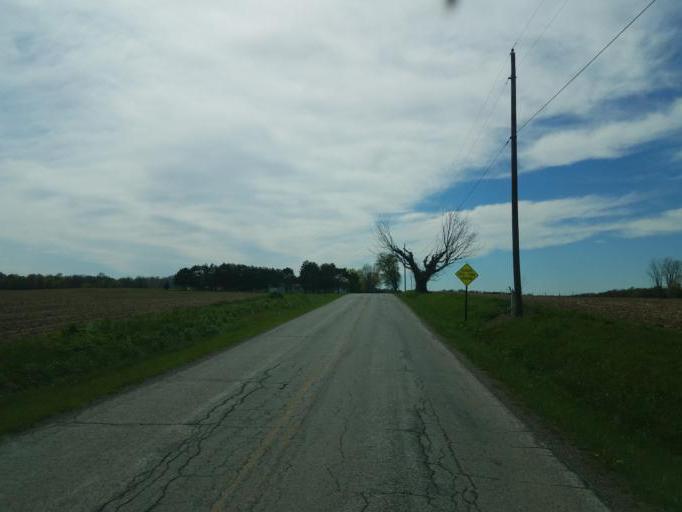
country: US
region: Ohio
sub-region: Richland County
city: Shelby
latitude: 40.9032
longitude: -82.5737
